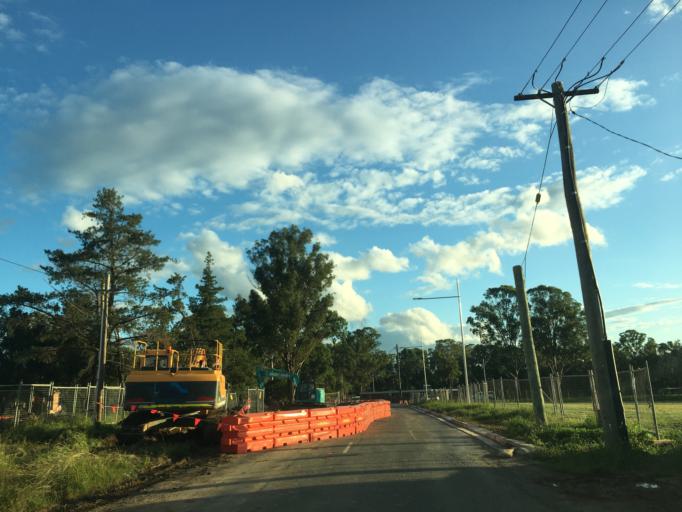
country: AU
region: New South Wales
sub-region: Campbelltown Municipality
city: Denham Court
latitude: -33.9699
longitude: 150.8065
